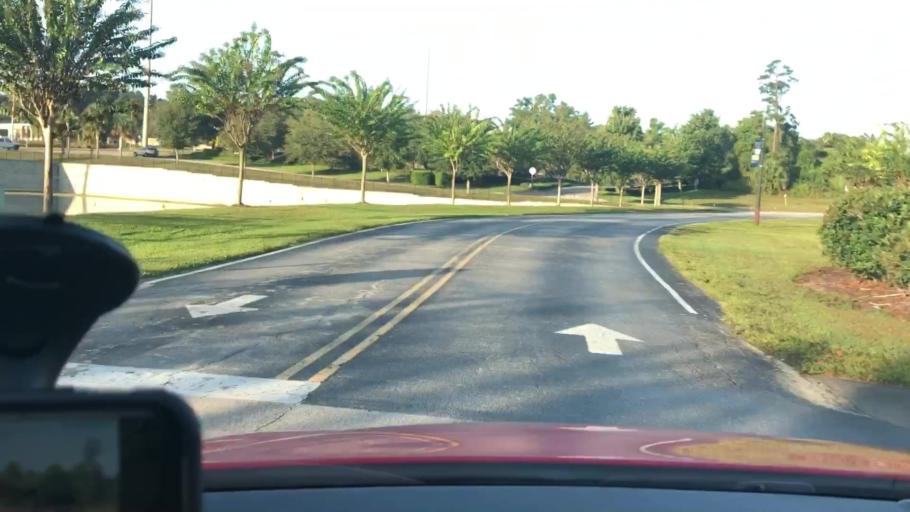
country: US
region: Florida
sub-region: Volusia County
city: Deltona
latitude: 28.9125
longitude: -81.2842
